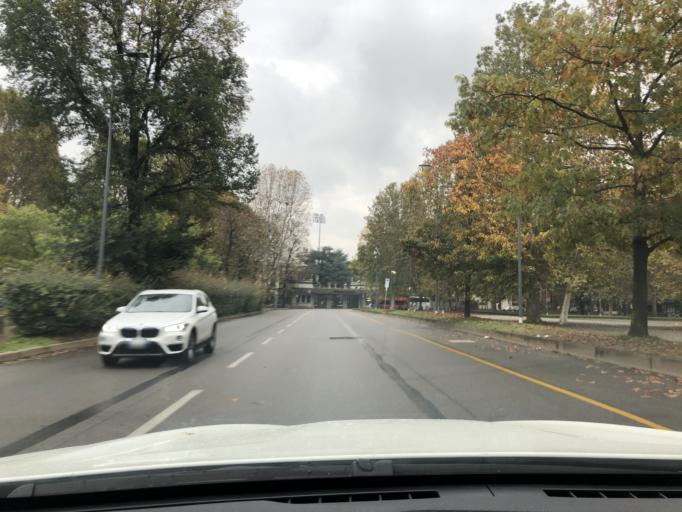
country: IT
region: Lombardy
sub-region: Citta metropolitana di Milano
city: Romano Banco
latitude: 45.4802
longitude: 9.1264
